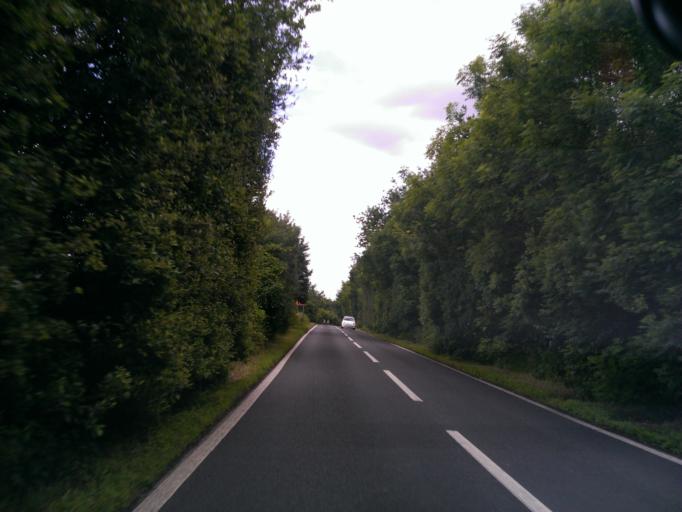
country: GB
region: England
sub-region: Essex
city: Witham
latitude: 51.8427
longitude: 0.6418
